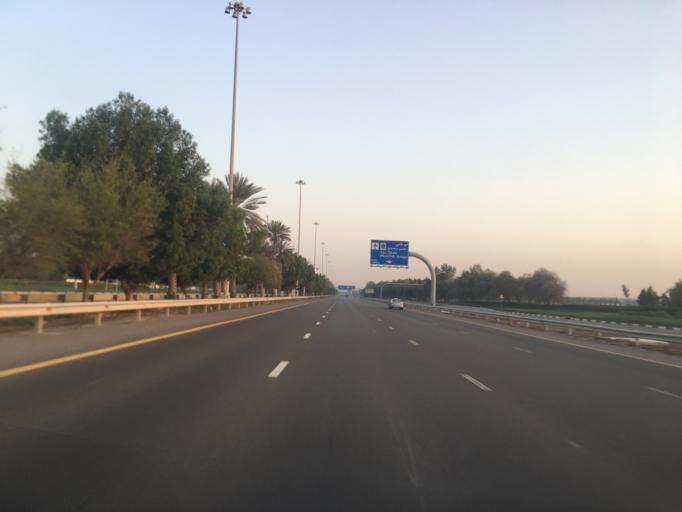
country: AE
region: Abu Dhabi
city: Abu Dhabi
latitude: 24.3767
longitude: 54.5510
